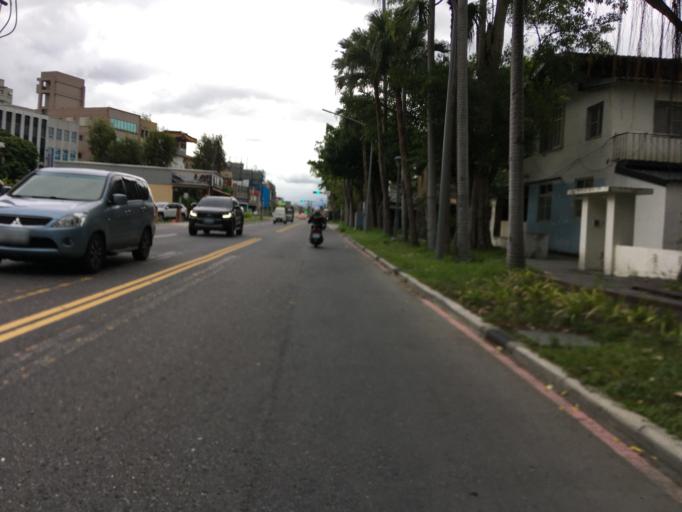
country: TW
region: Taiwan
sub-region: Yilan
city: Yilan
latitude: 24.6844
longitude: 121.7712
